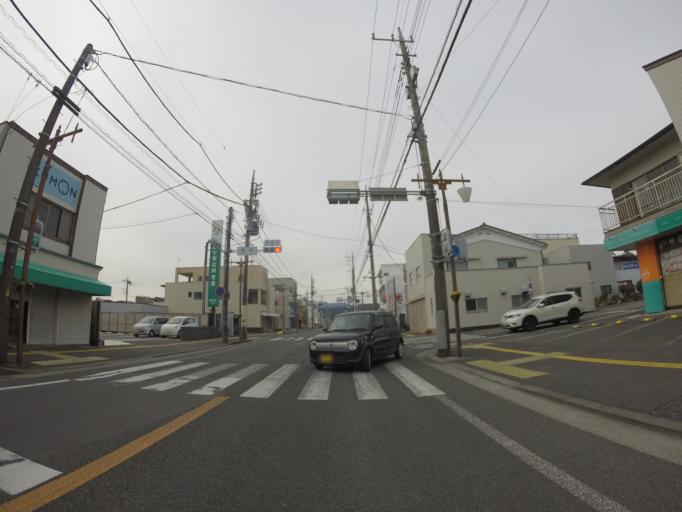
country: JP
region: Shizuoka
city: Fujinomiya
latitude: 35.2241
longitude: 138.6189
